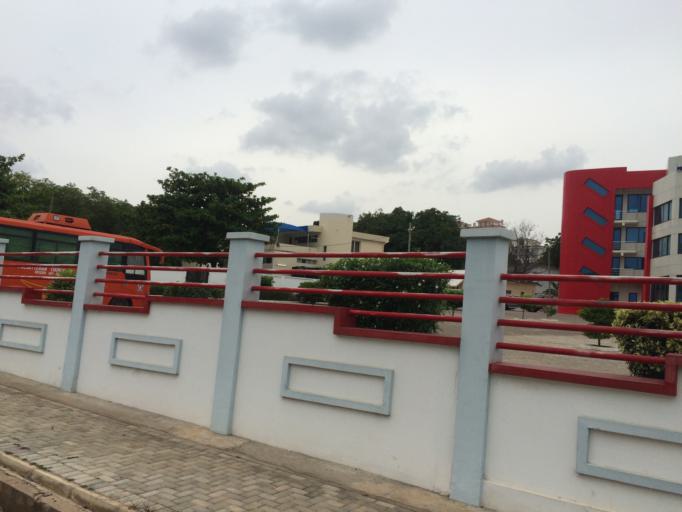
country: GH
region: Greater Accra
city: Accra
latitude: 5.5593
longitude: -0.1841
